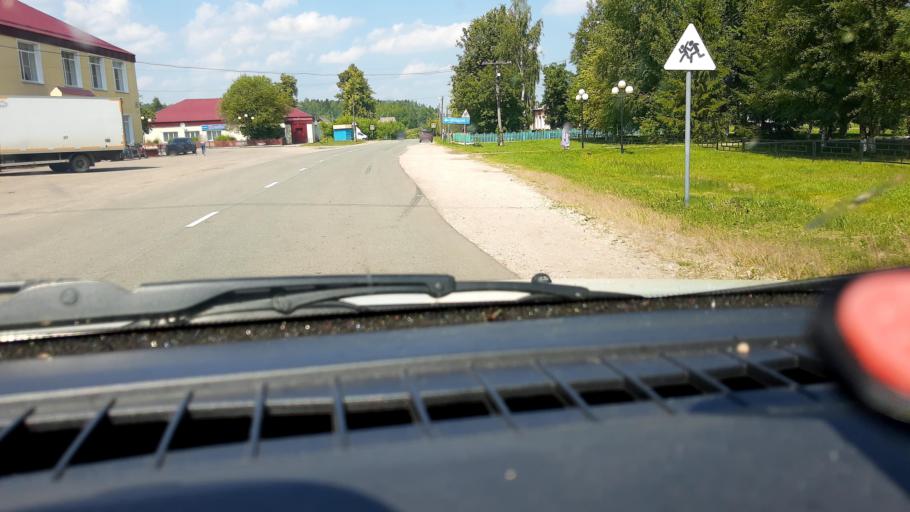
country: RU
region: Nizjnij Novgorod
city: Sharanga
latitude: 57.0505
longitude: 46.5462
